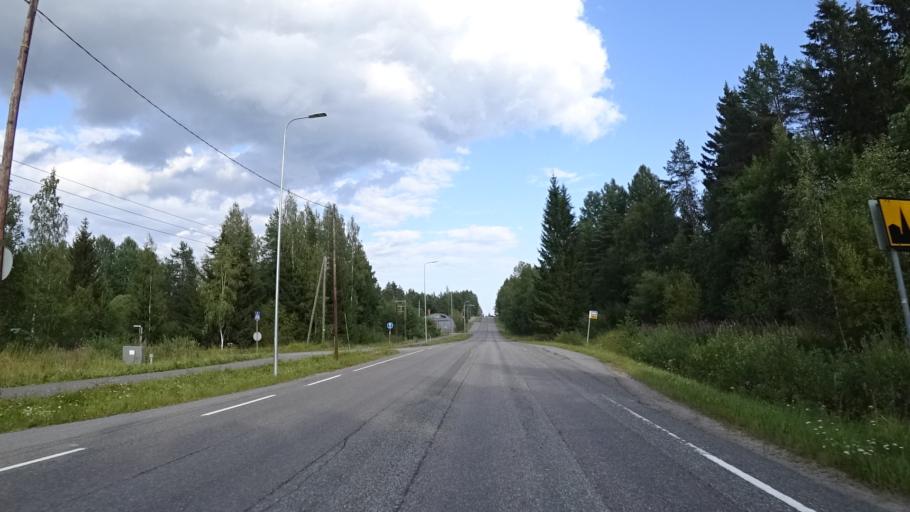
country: FI
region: South Karelia
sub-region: Imatra
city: Imatra
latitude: 61.1731
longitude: 28.7327
